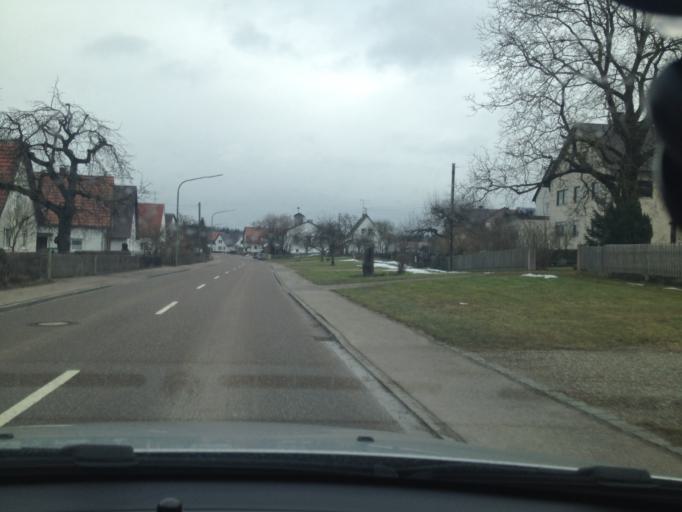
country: DE
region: Bavaria
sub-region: Swabia
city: Landensberg
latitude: 48.4416
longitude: 10.5583
